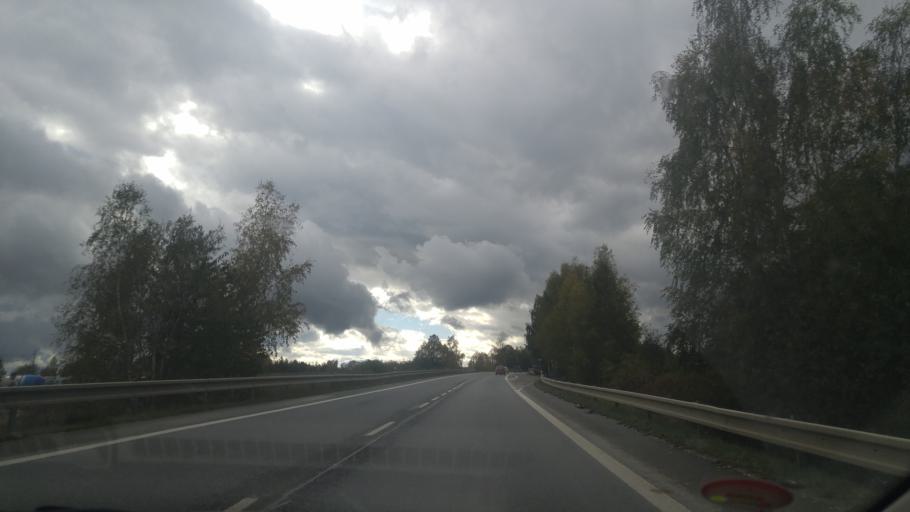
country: CZ
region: Jihocesky
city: Sevetin
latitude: 49.1277
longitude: 14.6054
